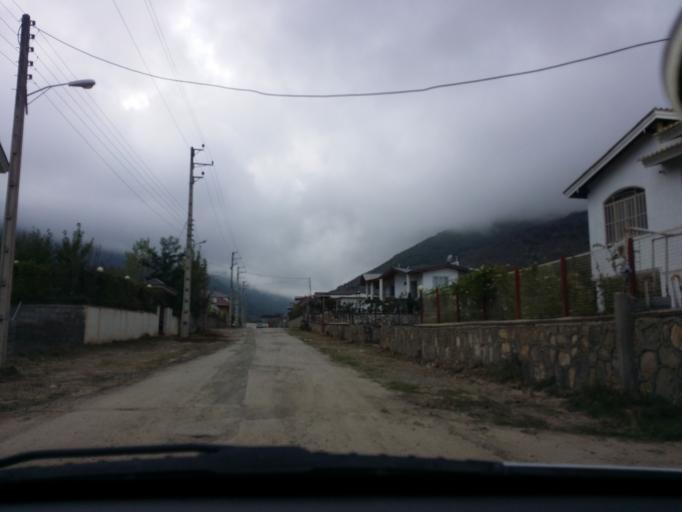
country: IR
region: Mazandaran
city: `Abbasabad
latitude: 36.4891
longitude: 51.1368
